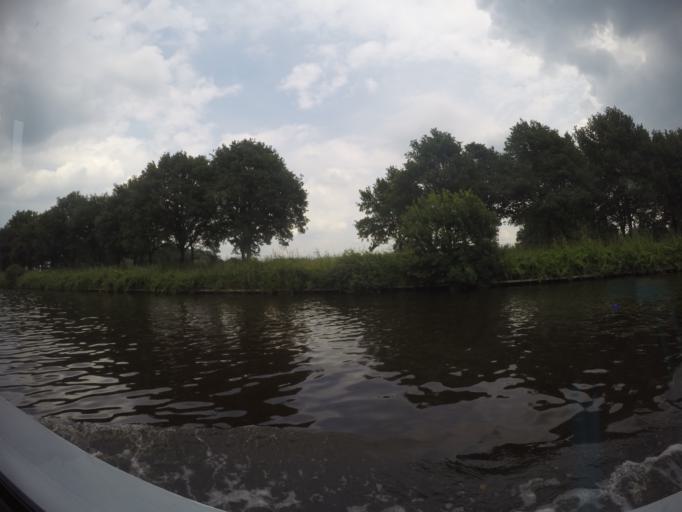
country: NL
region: Overijssel
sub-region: Gemeente Hof van Twente
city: Hengevelde
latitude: 52.2579
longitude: 6.6472
